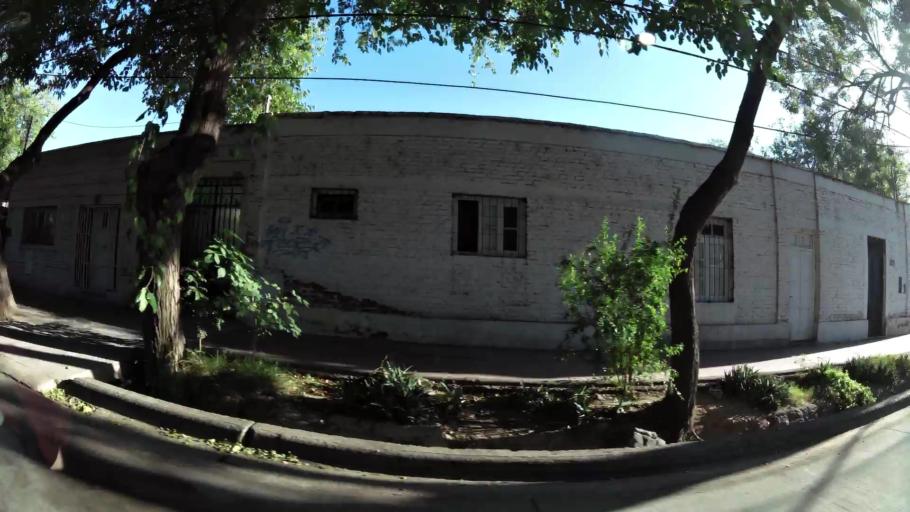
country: AR
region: Mendoza
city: Mendoza
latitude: -32.8722
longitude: -68.8211
